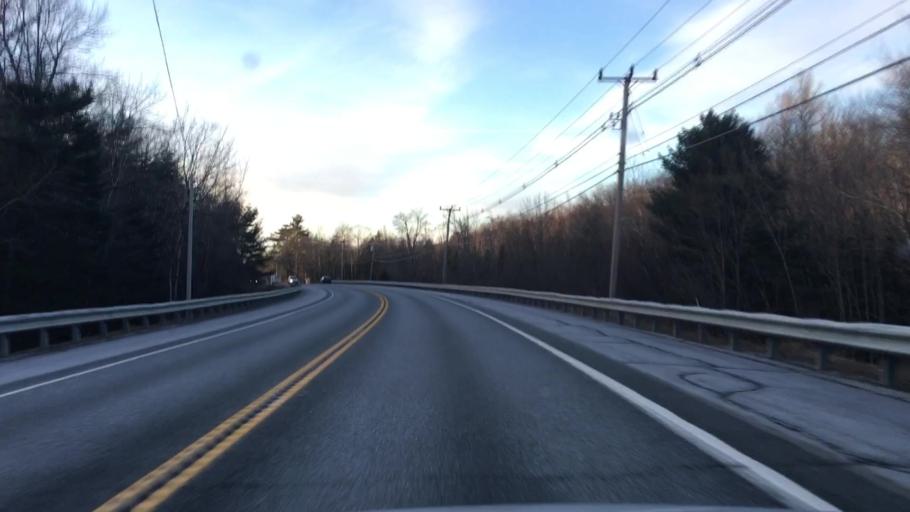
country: US
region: Maine
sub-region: Hancock County
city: Dedham
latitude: 44.7165
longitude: -68.6066
